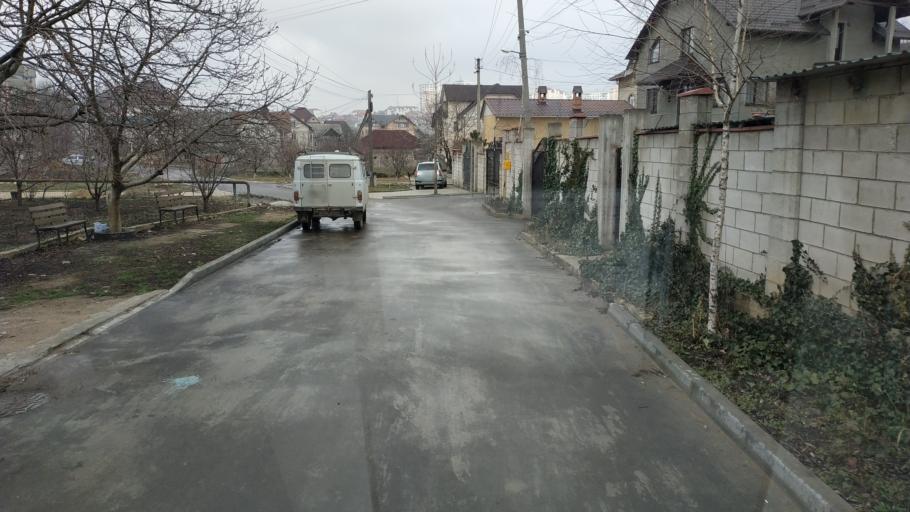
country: MD
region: Chisinau
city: Vatra
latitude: 47.0333
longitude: 28.7568
